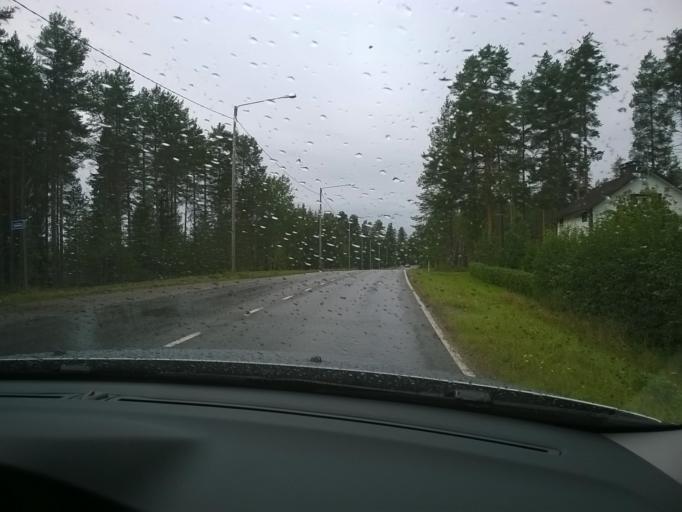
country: FI
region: Kainuu
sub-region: Kehys-Kainuu
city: Kuhmo
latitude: 64.1210
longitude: 29.5447
